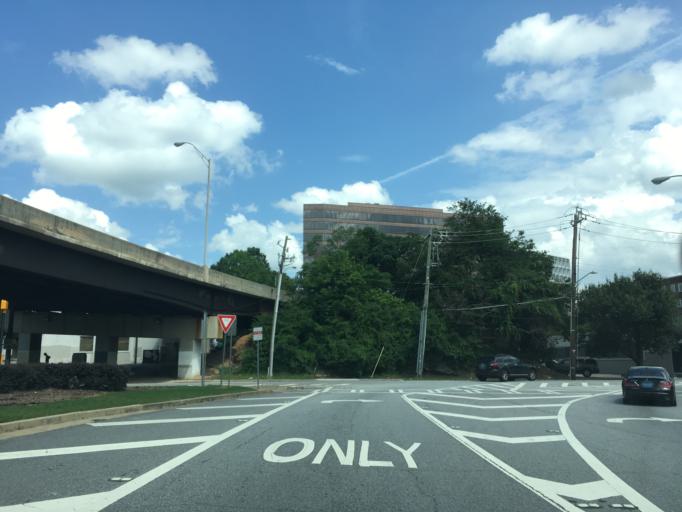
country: US
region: Georgia
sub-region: Fulton County
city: Atlanta
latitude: 33.7955
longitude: -84.3895
